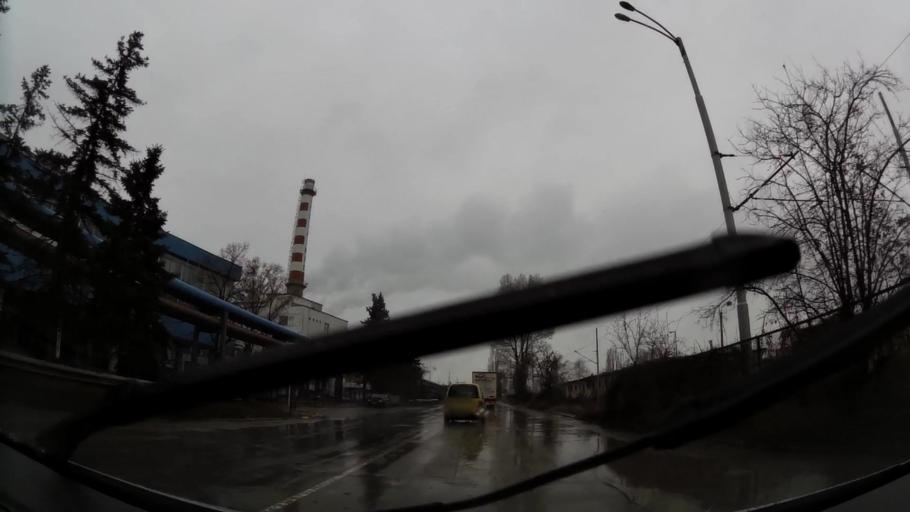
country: BG
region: Sofia-Capital
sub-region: Stolichna Obshtina
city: Sofia
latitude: 42.6584
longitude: 23.4150
